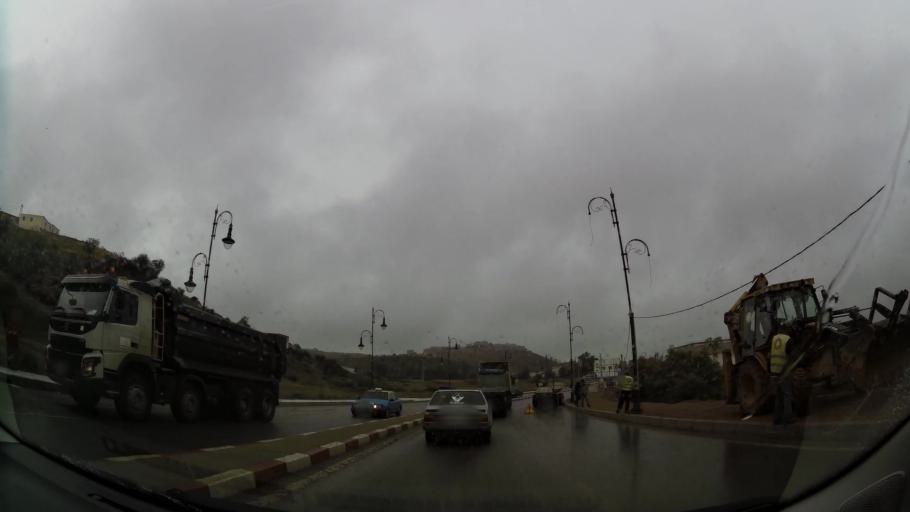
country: MA
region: Taza-Al Hoceima-Taounate
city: Imzourene
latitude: 35.1598
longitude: -3.8537
